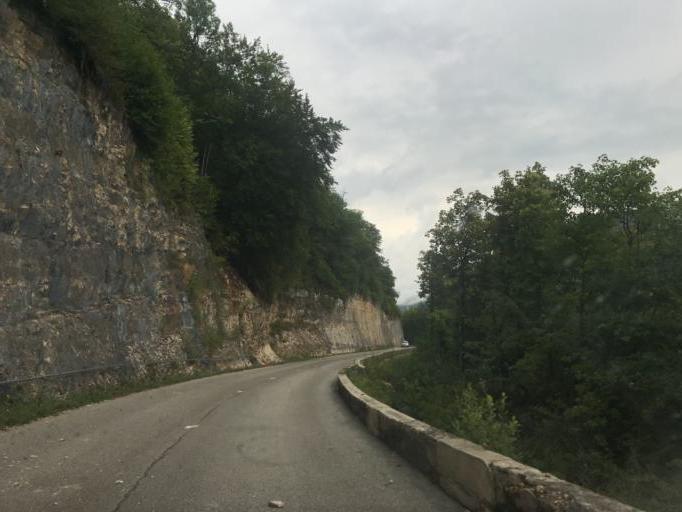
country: FR
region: Franche-Comte
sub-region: Departement du Jura
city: Lavans-les-Saint-Claude
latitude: 46.3378
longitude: 5.7666
